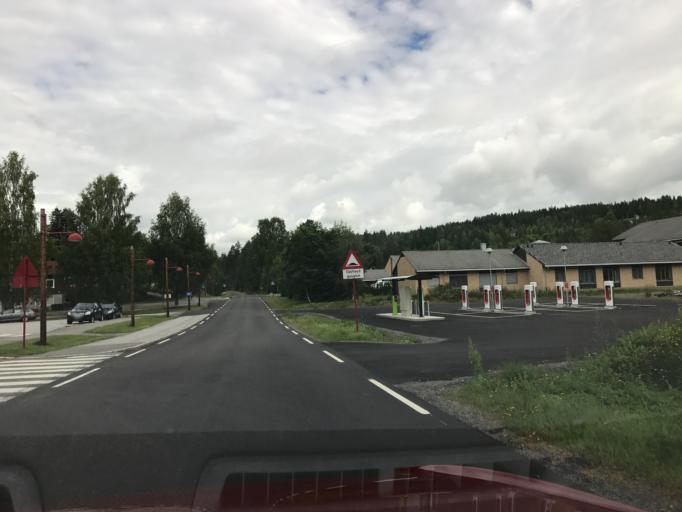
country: NO
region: Buskerud
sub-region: Flesberg
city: Lampeland
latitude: 59.8358
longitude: 9.5791
